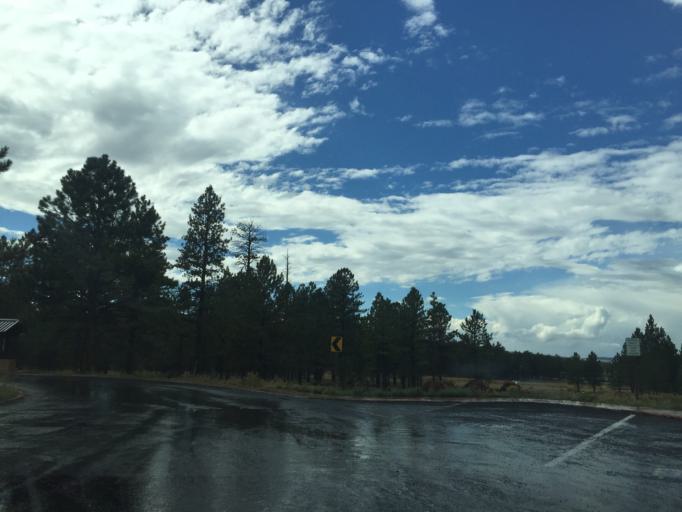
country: US
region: Utah
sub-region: Garfield County
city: Panguitch
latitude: 37.6403
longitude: -112.1704
